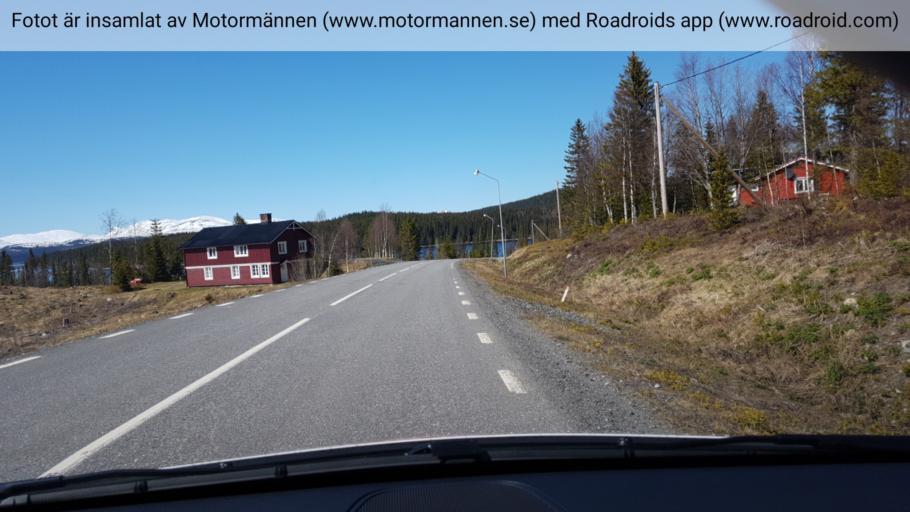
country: SE
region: Jaemtland
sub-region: Are Kommun
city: Are
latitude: 63.6637
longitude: 13.0497
